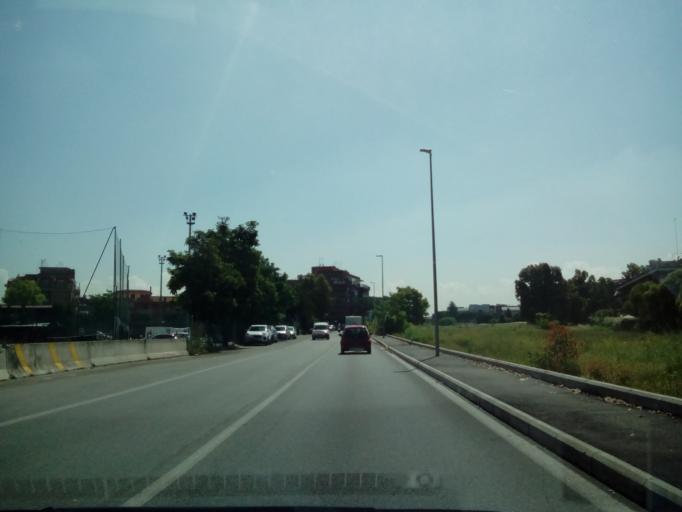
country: IT
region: Latium
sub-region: Citta metropolitana di Roma Capitale
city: Rome
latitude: 41.8918
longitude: 12.5825
